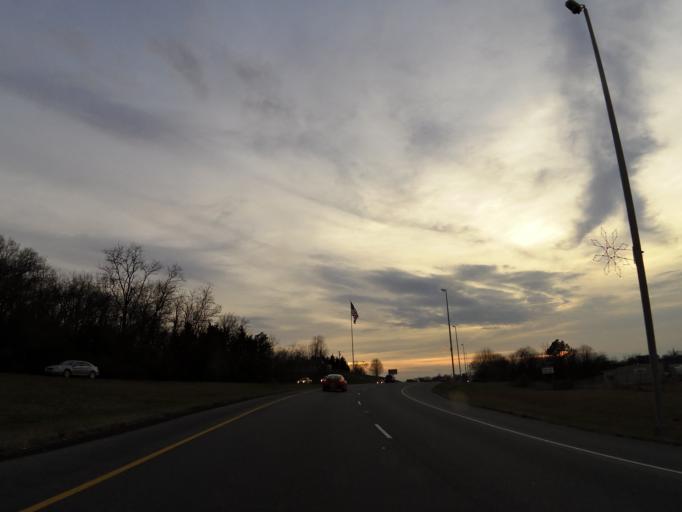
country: US
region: Tennessee
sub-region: Monroe County
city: Madisonville
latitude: 35.5215
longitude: -84.3539
